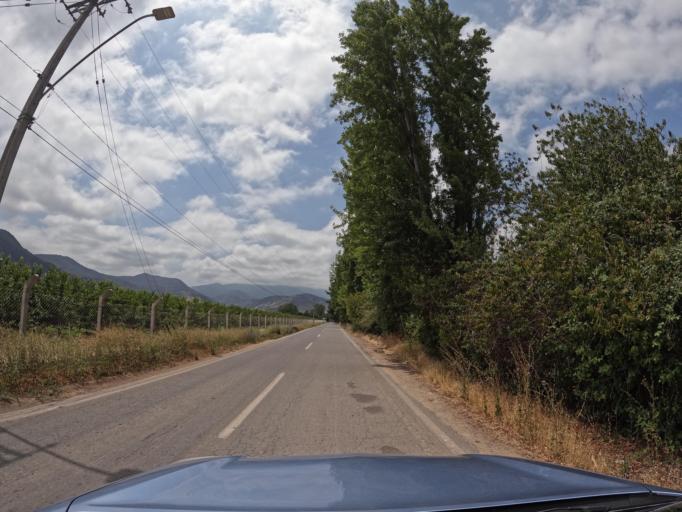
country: CL
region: O'Higgins
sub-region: Provincia de Colchagua
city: Chimbarongo
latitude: -34.7464
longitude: -70.9602
